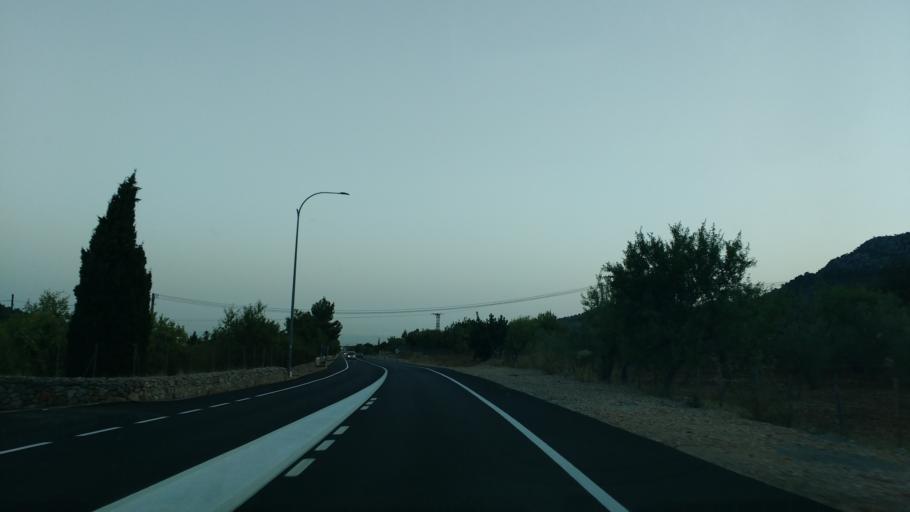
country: ES
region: Balearic Islands
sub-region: Illes Balears
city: Bunyola
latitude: 39.6945
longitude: 2.6865
